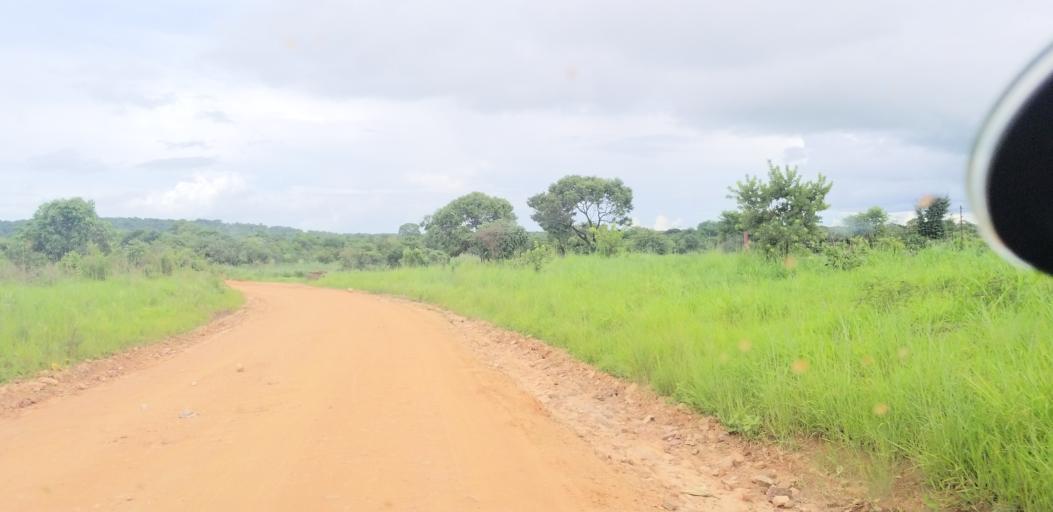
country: ZM
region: Lusaka
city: Lusaka
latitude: -15.1964
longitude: 28.4430
